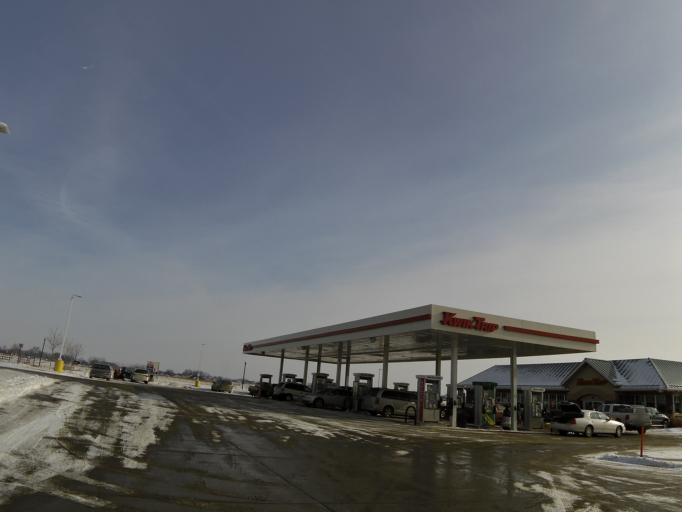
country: US
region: Minnesota
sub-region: McLeod County
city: Hutchinson
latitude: 44.8706
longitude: -94.3747
